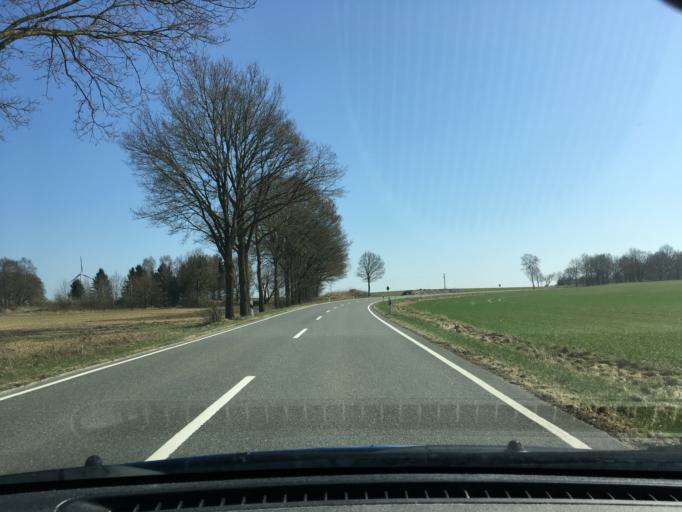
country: DE
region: Lower Saxony
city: Rehlingen
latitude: 53.1049
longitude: 10.2582
